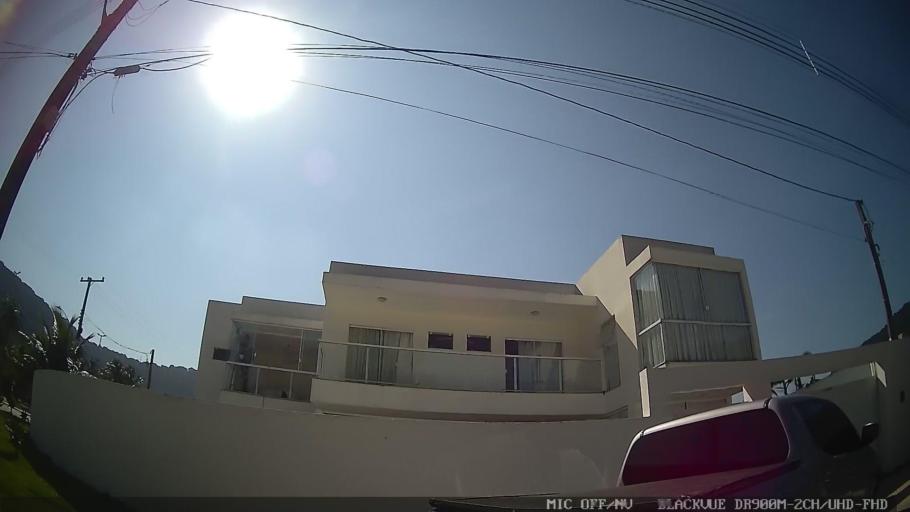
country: BR
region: Sao Paulo
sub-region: Guaruja
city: Guaruja
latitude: -24.0179
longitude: -46.2909
